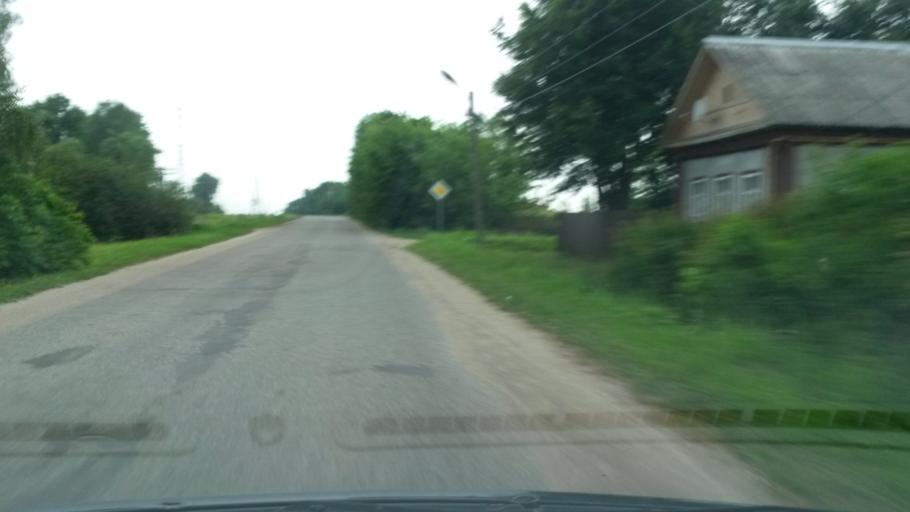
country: RU
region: Ivanovo
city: Pistsovo
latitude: 57.1784
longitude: 40.5222
